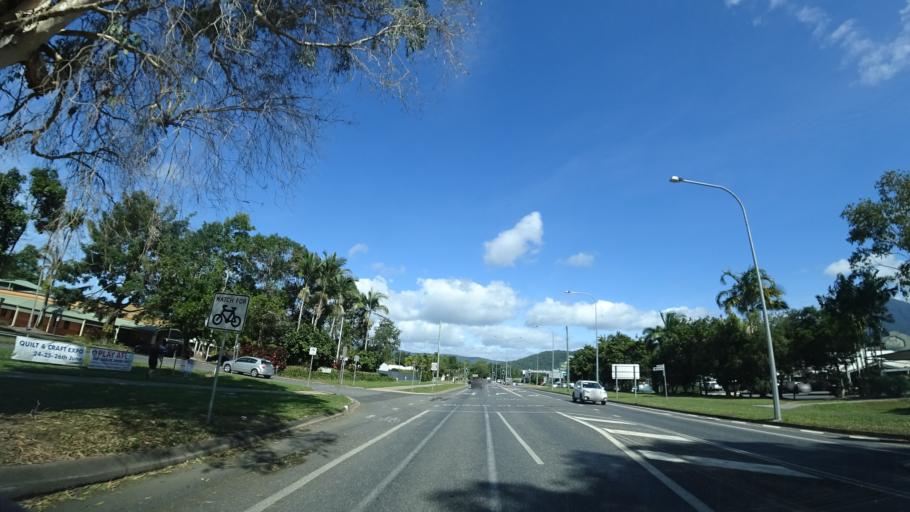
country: AU
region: Queensland
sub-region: Cairns
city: Port Douglas
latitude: -16.4647
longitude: 145.3733
